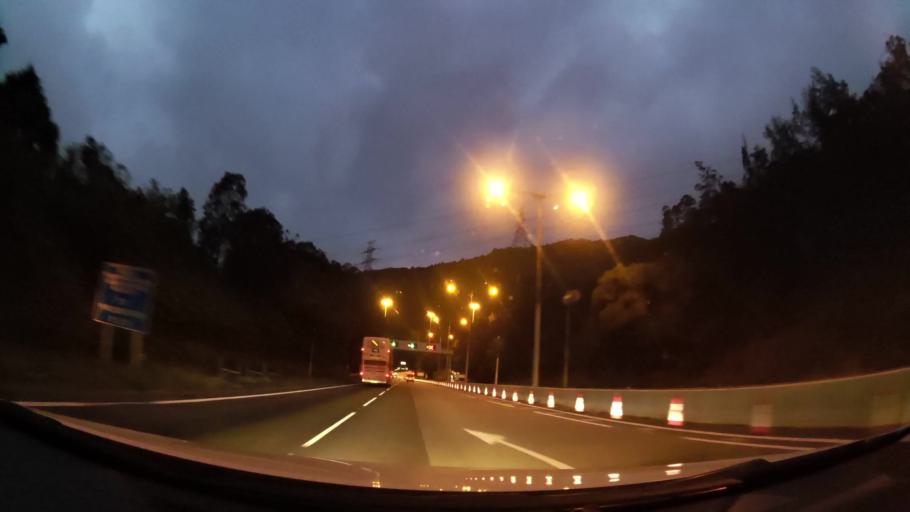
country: HK
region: Sha Tin
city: Sha Tin
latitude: 22.3810
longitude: 114.1677
